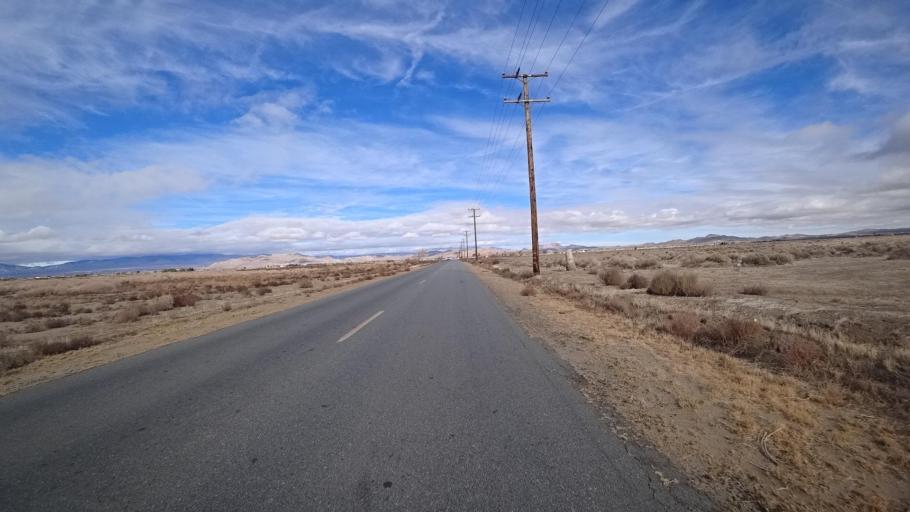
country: US
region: California
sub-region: Kern County
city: Rosamond
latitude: 34.8223
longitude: -118.2377
